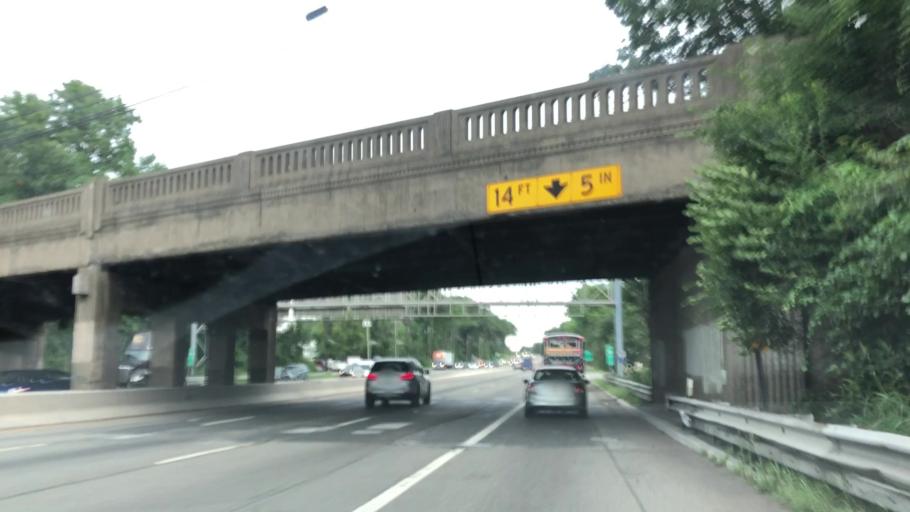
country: US
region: New Jersey
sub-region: Passaic County
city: Clifton
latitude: 40.8492
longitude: -74.1726
